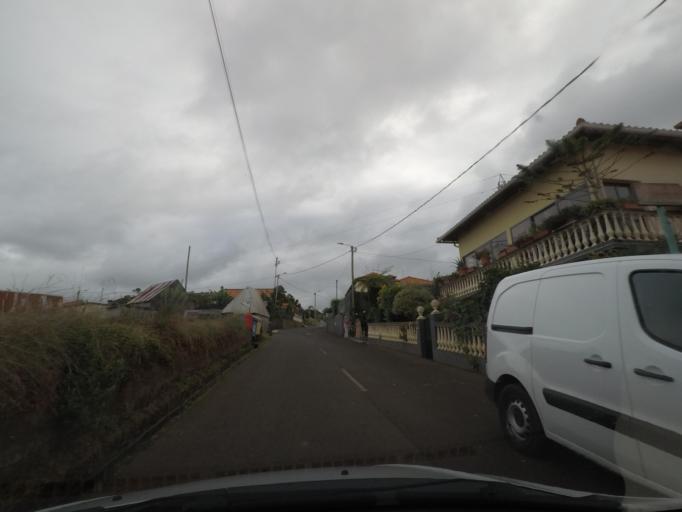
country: PT
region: Madeira
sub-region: Santana
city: Santana
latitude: 32.7888
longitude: -16.8736
